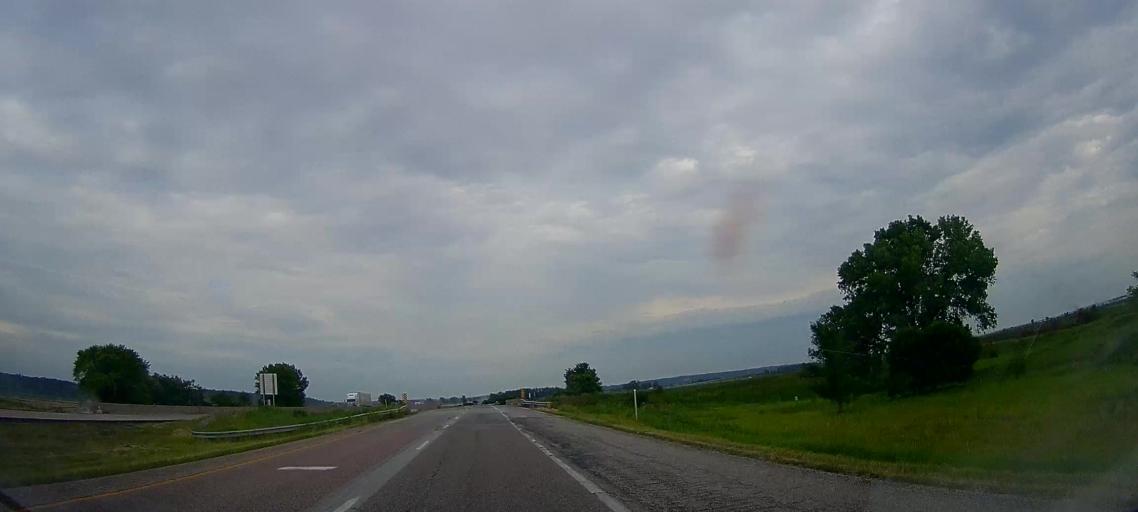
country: US
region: Iowa
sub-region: Harrison County
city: Missouri Valley
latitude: 41.5743
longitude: -95.9288
